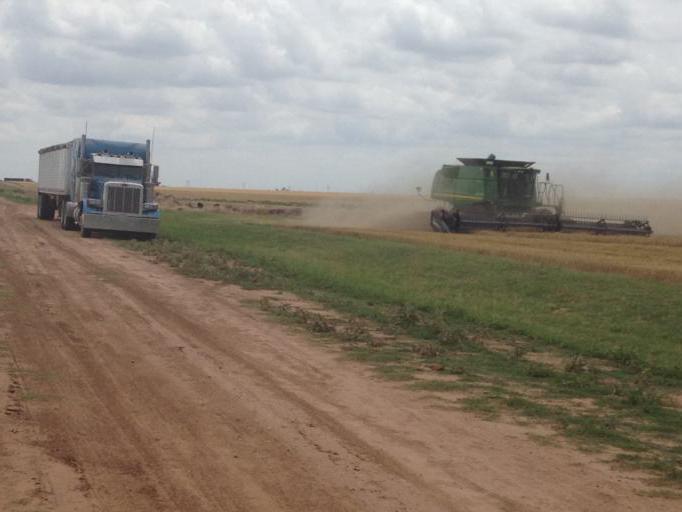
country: US
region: Oklahoma
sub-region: Alfalfa County
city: Helena
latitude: 36.6450
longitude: -98.0375
